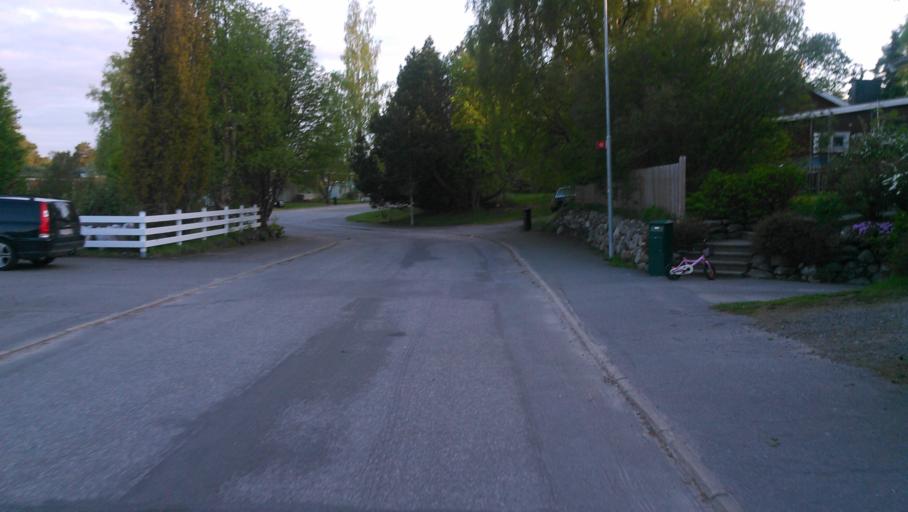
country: SE
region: Vaesterbotten
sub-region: Umea Kommun
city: Umea
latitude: 63.8302
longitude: 20.3075
